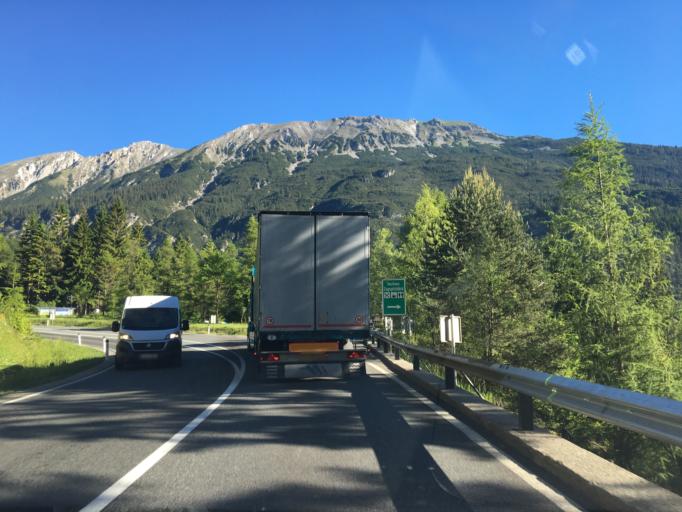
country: AT
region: Tyrol
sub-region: Politischer Bezirk Imst
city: Nassereith
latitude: 47.3608
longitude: 10.8449
